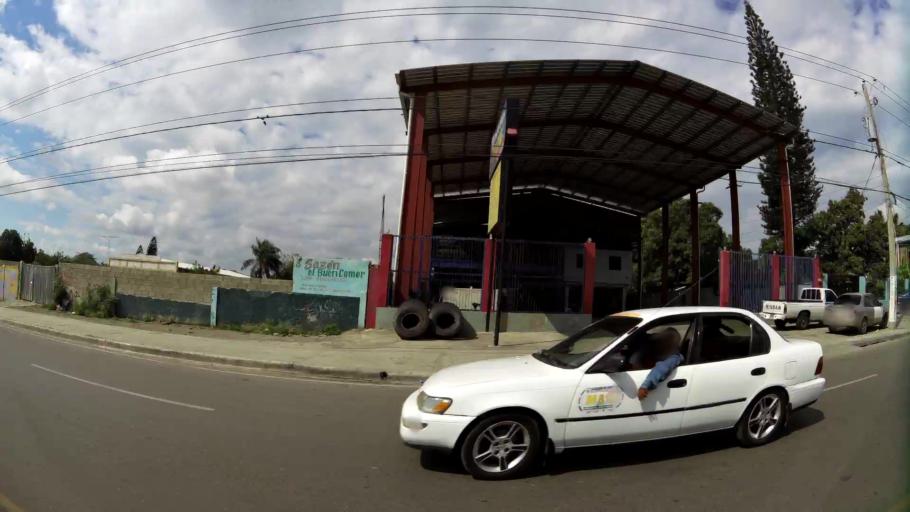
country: DO
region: Santiago
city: Santiago de los Caballeros
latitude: 19.4804
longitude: -70.7269
